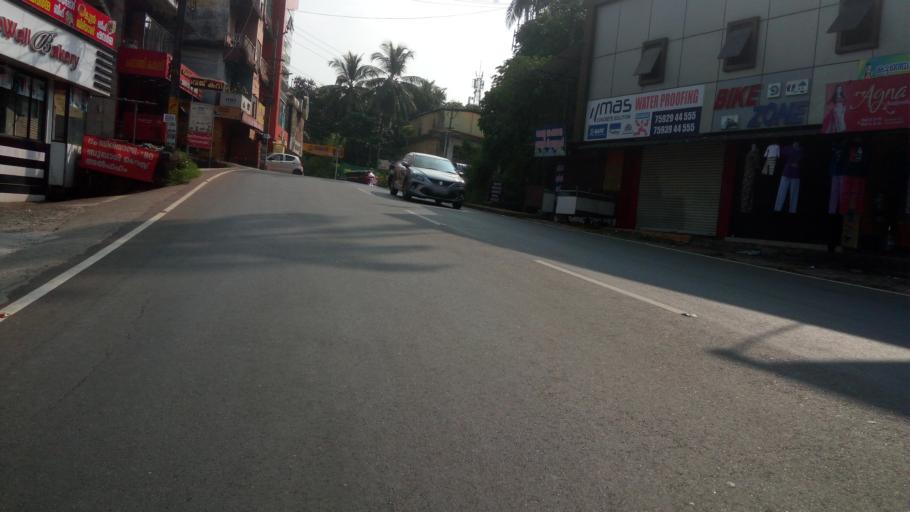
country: IN
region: Kerala
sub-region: Malappuram
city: Malappuram
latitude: 11.0029
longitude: 76.0094
